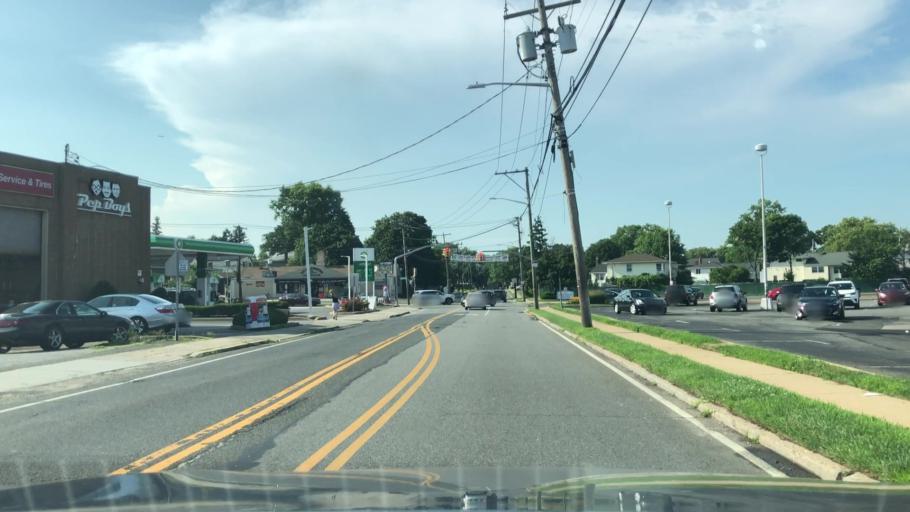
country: US
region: New York
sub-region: Nassau County
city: Franklin Square
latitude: 40.7125
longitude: -73.6768
